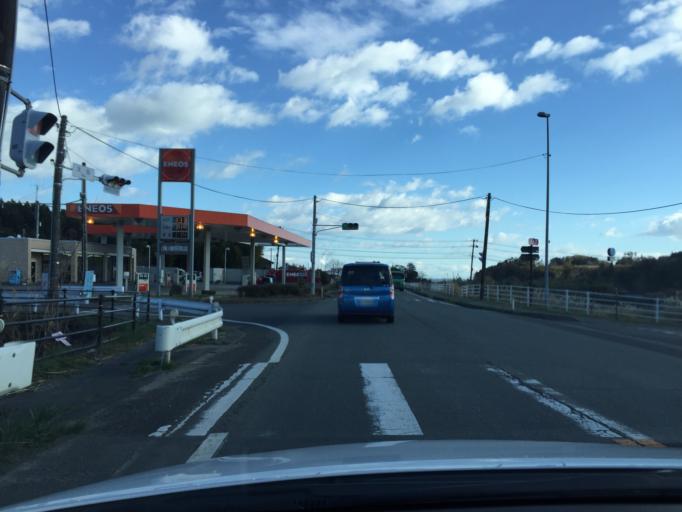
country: JP
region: Fukushima
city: Namie
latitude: 37.3209
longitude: 141.0074
